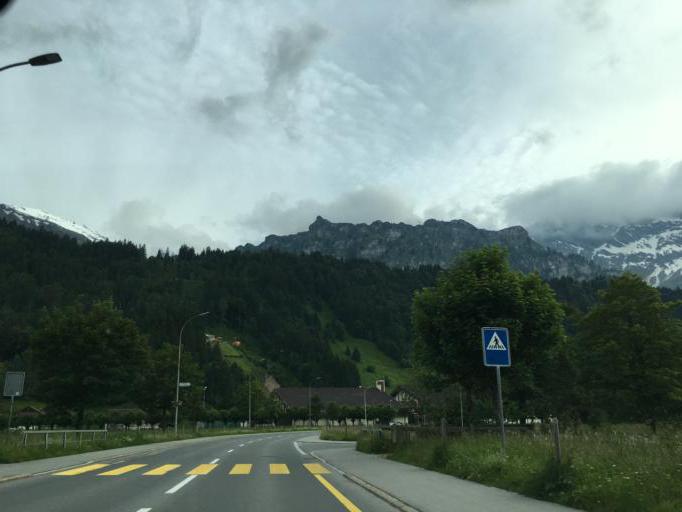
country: CH
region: Obwalden
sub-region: Obwalden
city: Engelberg
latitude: 46.8195
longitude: 8.4067
